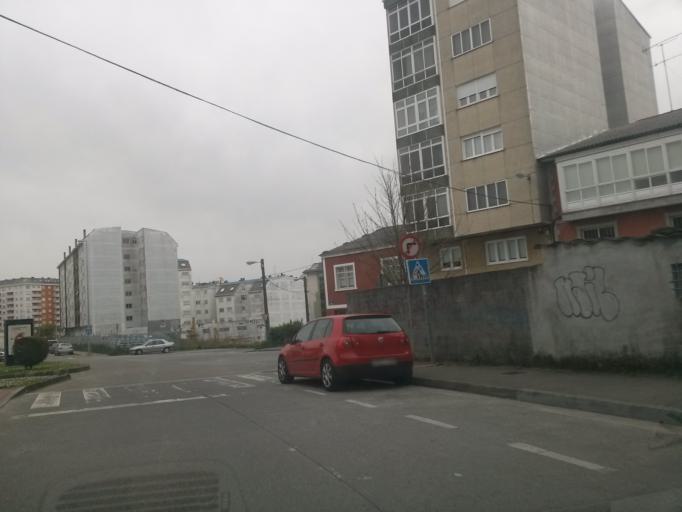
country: ES
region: Galicia
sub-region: Provincia de Lugo
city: Lugo
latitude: 43.0242
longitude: -7.5702
